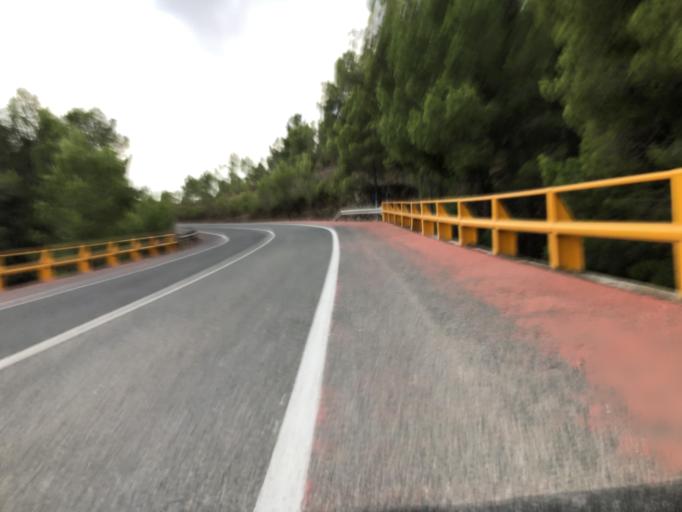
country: ES
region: Valencia
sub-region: Provincia de Alicante
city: Polop
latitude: 38.6369
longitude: -0.1555
